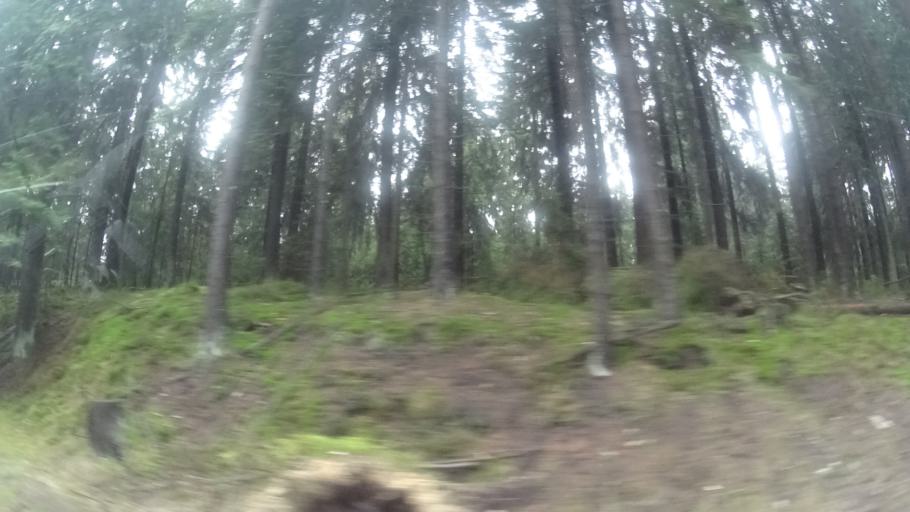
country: DE
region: Thuringia
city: Steinheid
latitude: 50.4839
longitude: 11.0976
